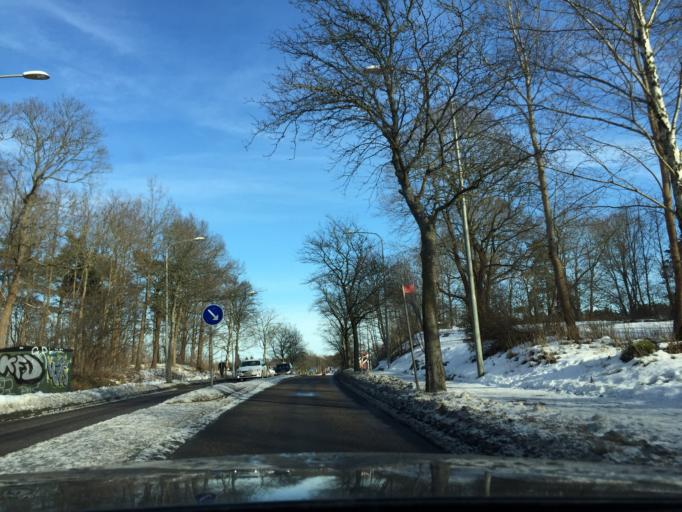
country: SE
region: Stockholm
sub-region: Stockholms Kommun
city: Bromma
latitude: 59.3494
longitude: 17.8972
